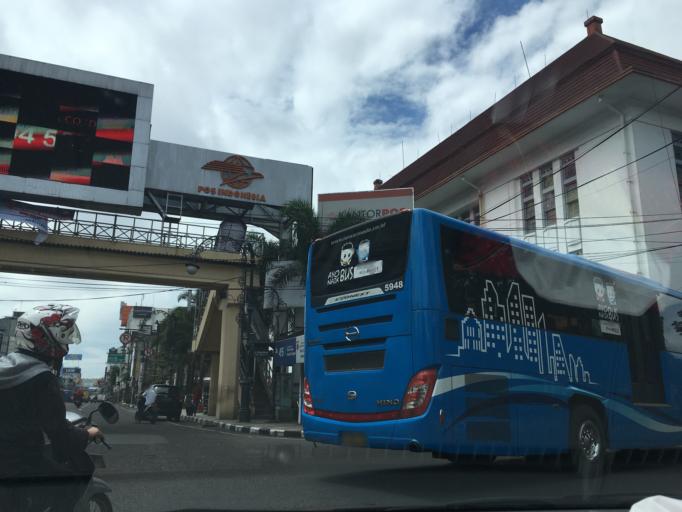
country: ID
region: West Java
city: Bandung
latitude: -6.9210
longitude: 107.6065
